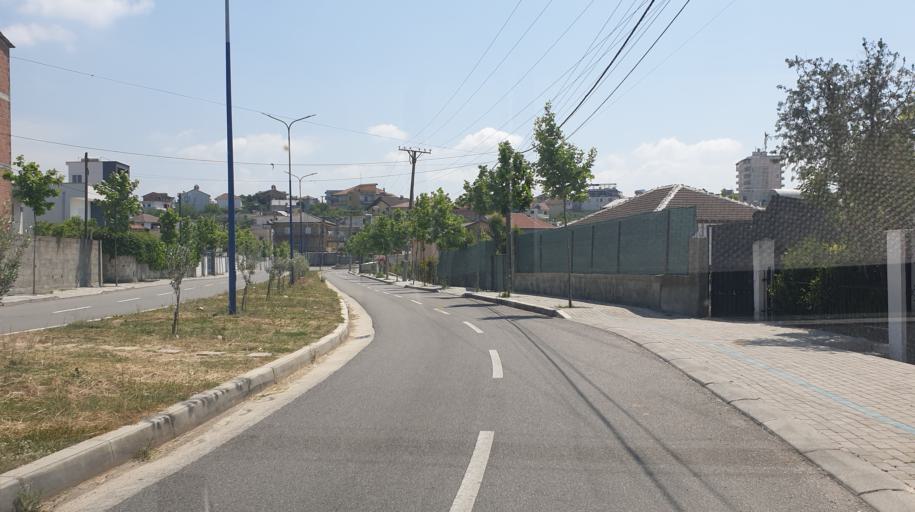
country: AL
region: Tirane
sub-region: Rrethi i Tiranes
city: Kamez
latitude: 41.3658
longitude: 19.7731
